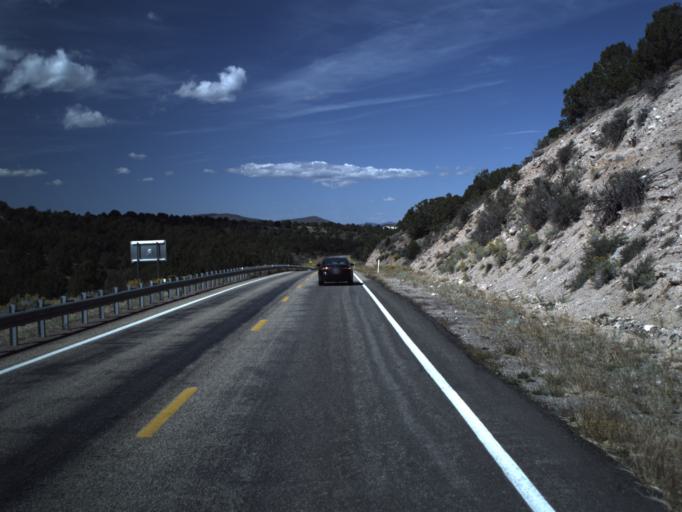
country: US
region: Utah
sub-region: Washington County
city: Enterprise
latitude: 37.5528
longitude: -113.6876
